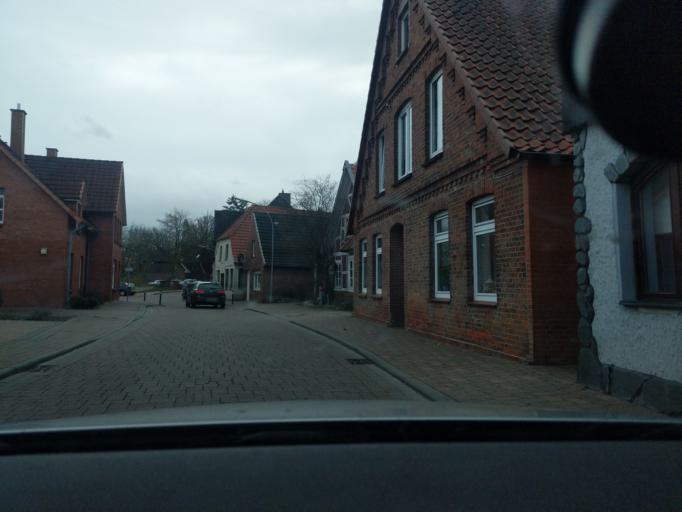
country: DE
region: Lower Saxony
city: Neuenkirchen
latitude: 53.5117
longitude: 9.5896
